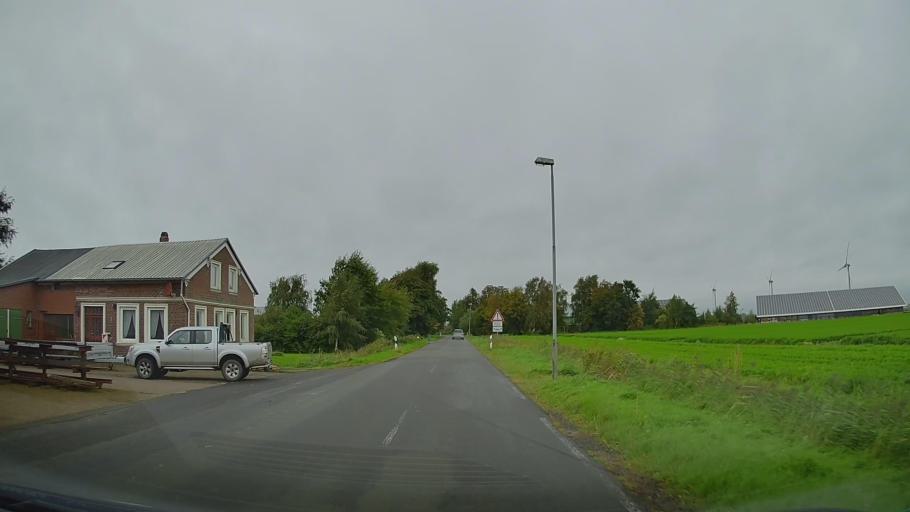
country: DE
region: Schleswig-Holstein
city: Diekhusen-Fahrstedt
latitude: 53.9169
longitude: 8.9968
